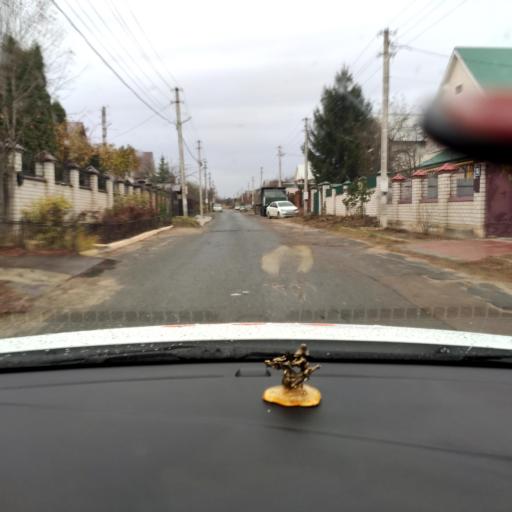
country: RU
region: Tatarstan
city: Vysokaya Gora
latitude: 55.8446
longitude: 49.2386
